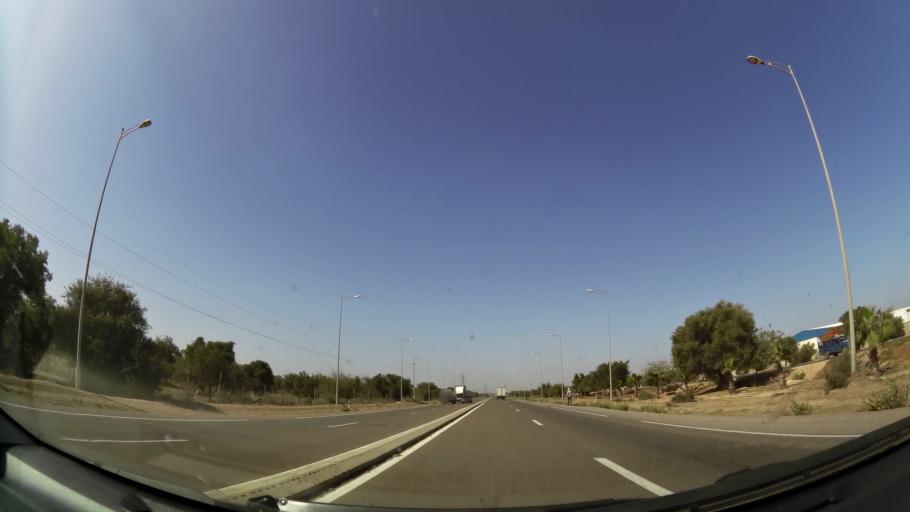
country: MA
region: Souss-Massa-Draa
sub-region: Inezgane-Ait Mellou
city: Inezgane
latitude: 30.3205
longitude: -9.4887
